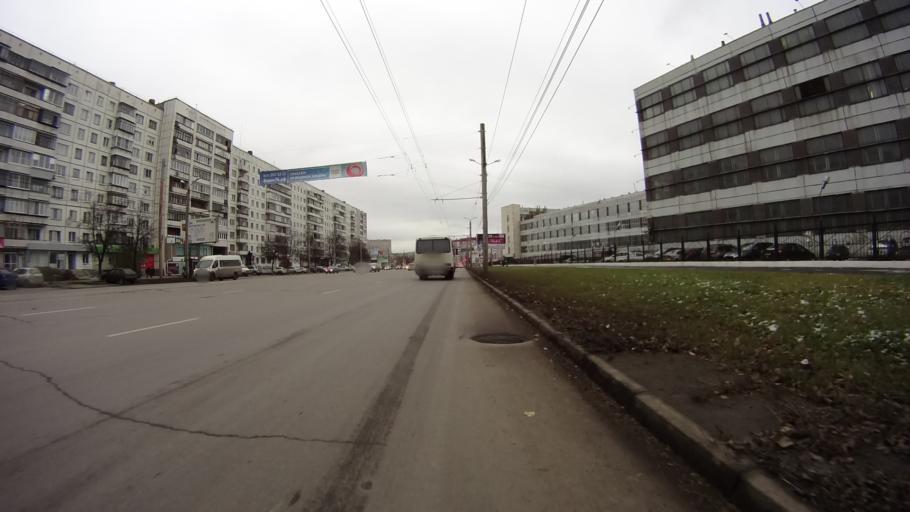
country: RU
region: Chelyabinsk
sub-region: Gorod Chelyabinsk
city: Chelyabinsk
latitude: 55.1932
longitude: 61.3579
